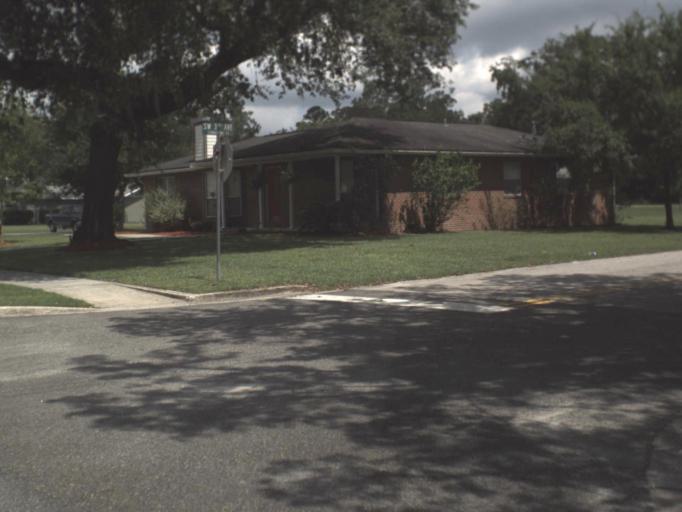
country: US
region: Florida
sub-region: Union County
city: Lake Butler
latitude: 30.0181
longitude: -82.3404
